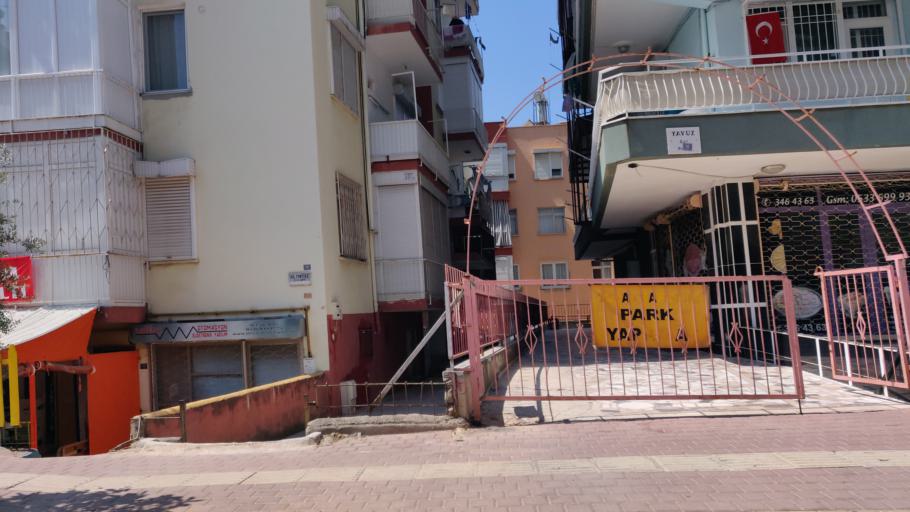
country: TR
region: Antalya
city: Antalya
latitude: 36.9086
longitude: 30.6836
